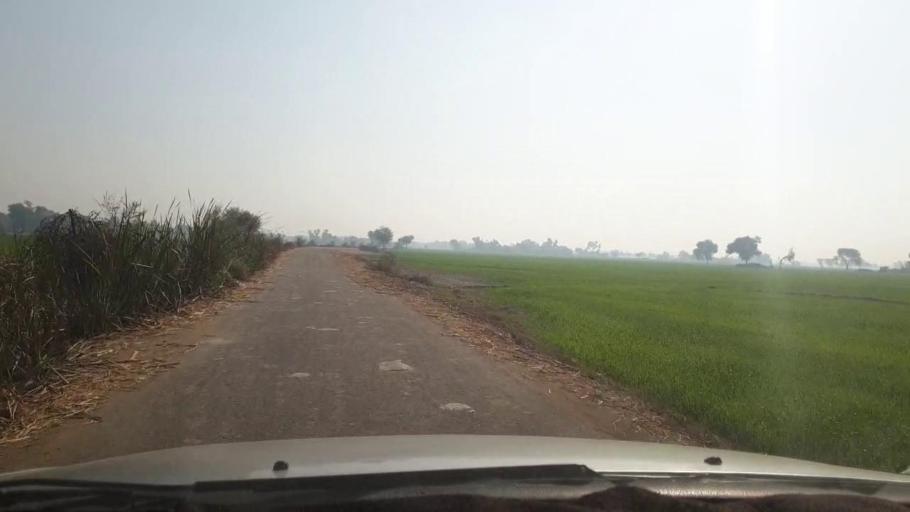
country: PK
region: Sindh
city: Khanpur
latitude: 27.7365
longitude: 69.5093
